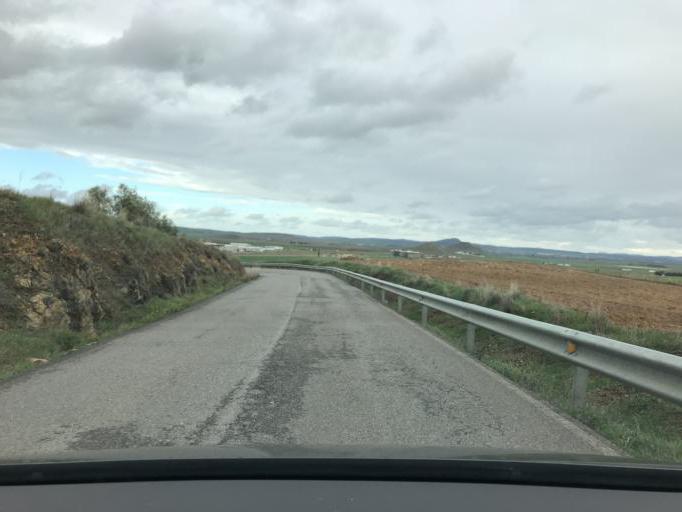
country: ES
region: Andalusia
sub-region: Province of Cordoba
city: Fuente Obejuna
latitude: 38.2699
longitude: -5.4118
